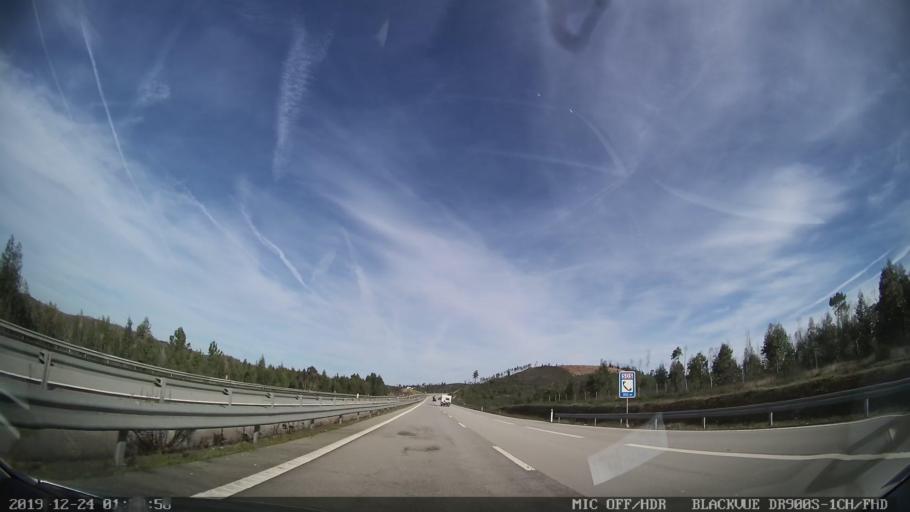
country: PT
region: Portalegre
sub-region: Gaviao
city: Gaviao
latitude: 39.5353
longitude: -7.8963
